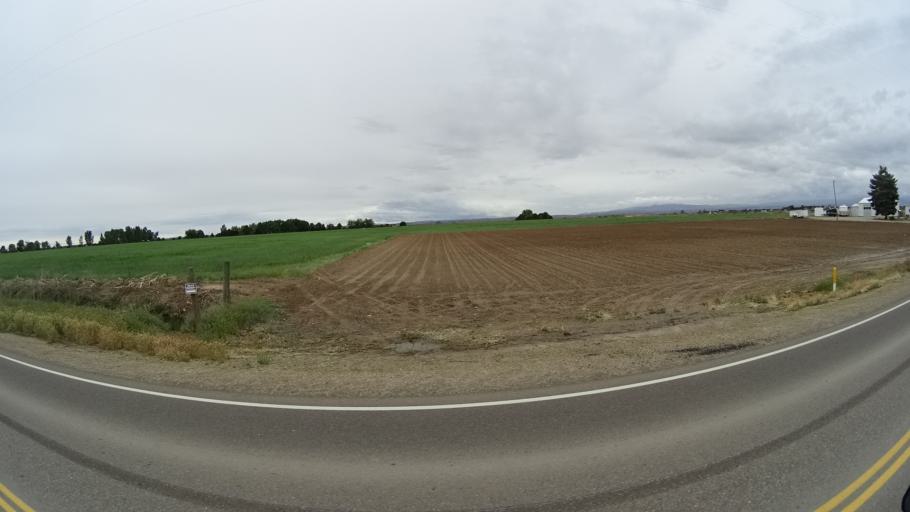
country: US
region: Idaho
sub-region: Ada County
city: Star
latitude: 43.6630
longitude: -116.4601
